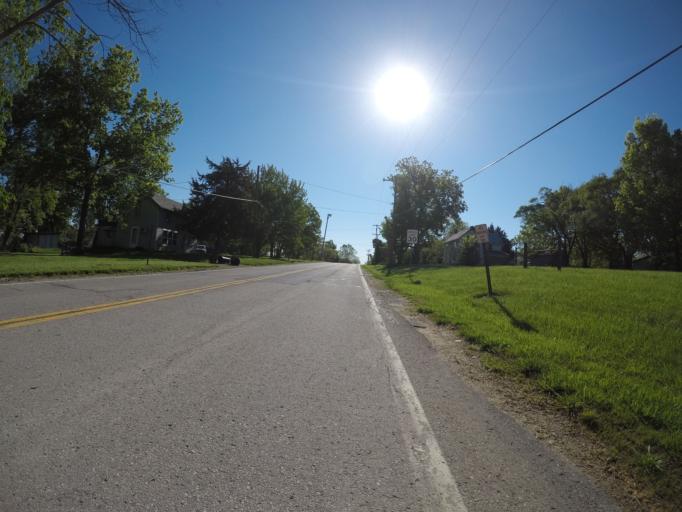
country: US
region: Kansas
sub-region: Douglas County
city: Lawrence
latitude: 39.0439
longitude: -95.3980
